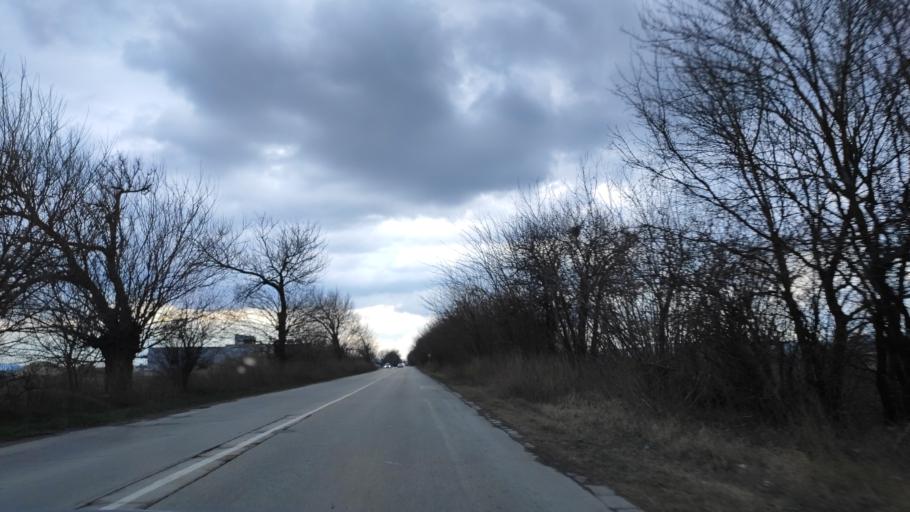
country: BG
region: Varna
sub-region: Obshtina Aksakovo
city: Aksakovo
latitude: 43.2280
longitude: 27.8472
